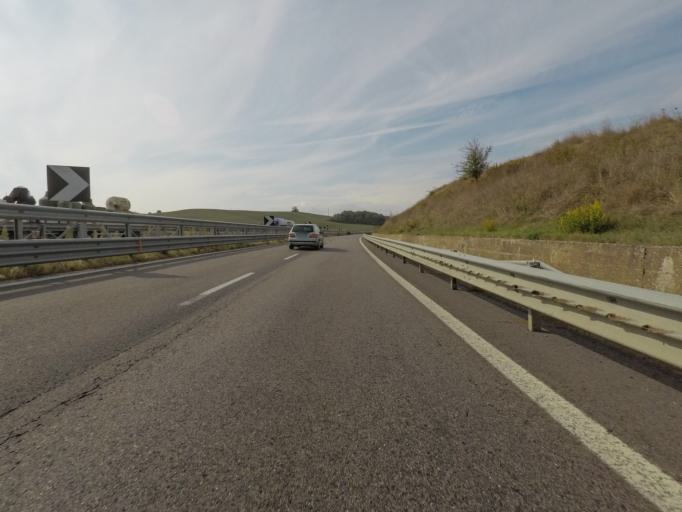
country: IT
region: Tuscany
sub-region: Provincia di Siena
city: Isola D'Arbia
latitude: 43.2575
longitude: 11.3250
